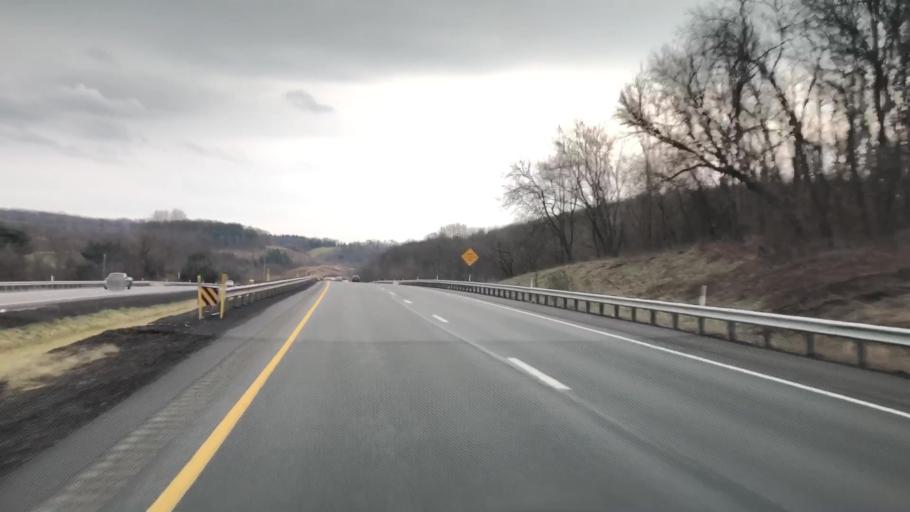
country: US
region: Pennsylvania
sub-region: Butler County
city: Zelienople
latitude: 40.8572
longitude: -80.1071
